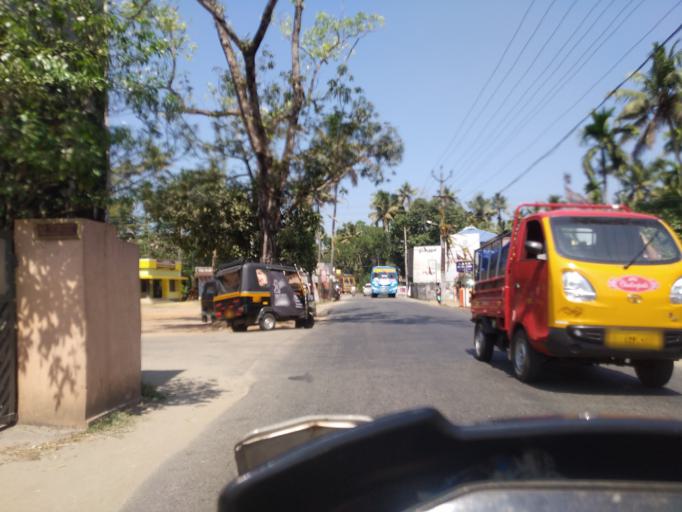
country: IN
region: Kerala
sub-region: Thrissur District
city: Kodungallur
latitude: 10.1672
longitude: 76.2131
